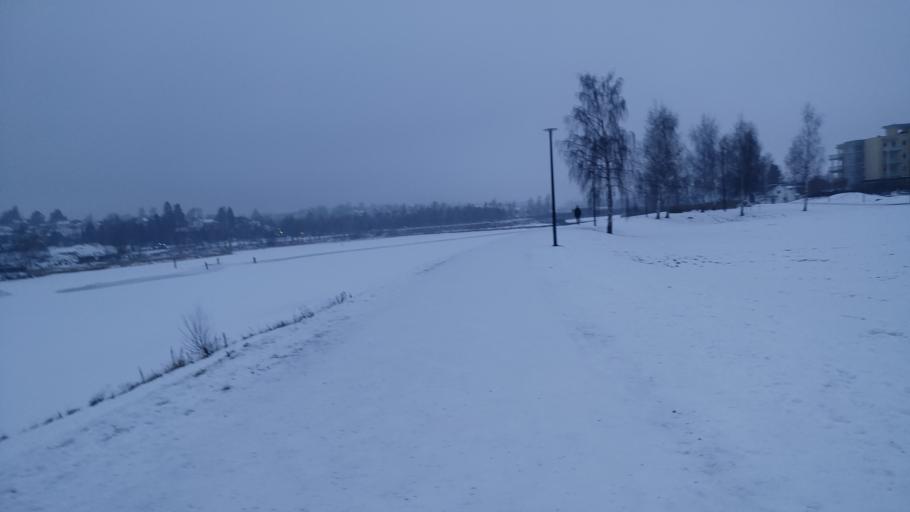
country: NO
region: Akershus
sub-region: Skedsmo
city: Lillestrom
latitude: 59.9547
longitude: 11.0329
